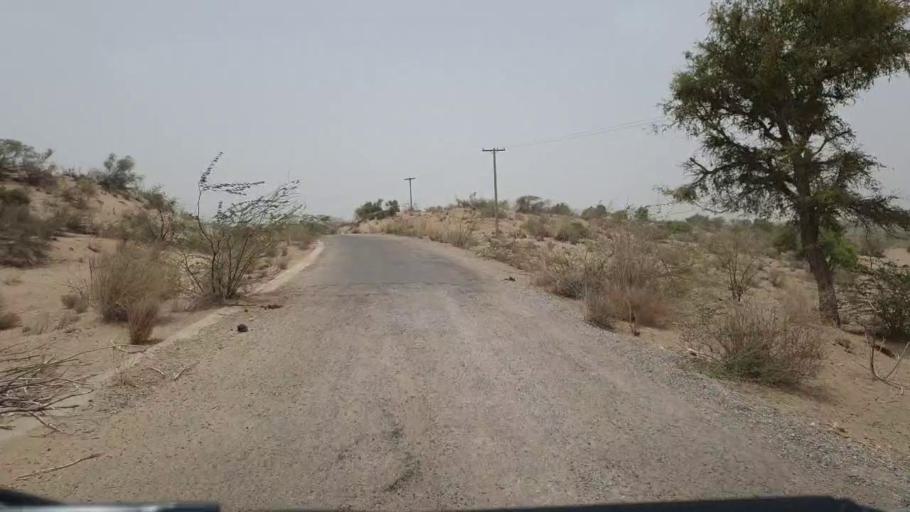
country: PK
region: Sindh
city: Naukot
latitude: 24.7552
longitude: 69.5525
